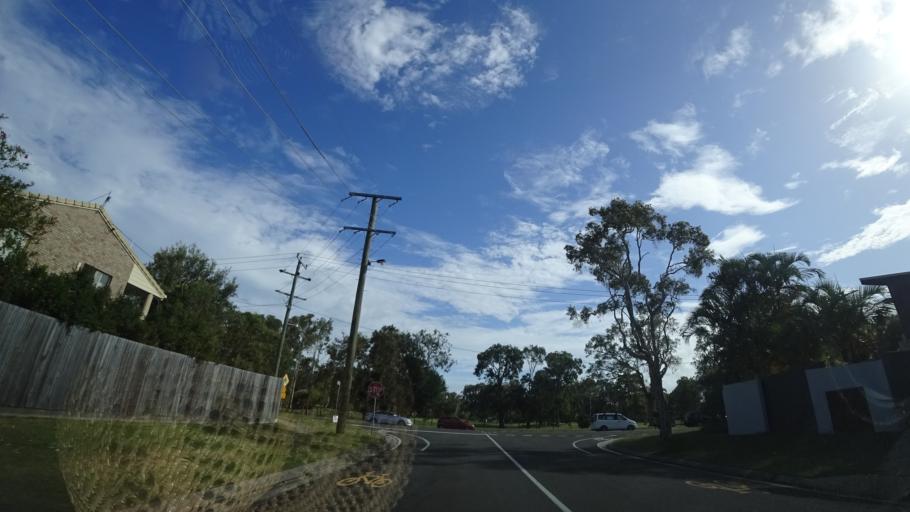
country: AU
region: Queensland
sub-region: Sunshine Coast
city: Coolum Beach
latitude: -26.5661
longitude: 153.0895
